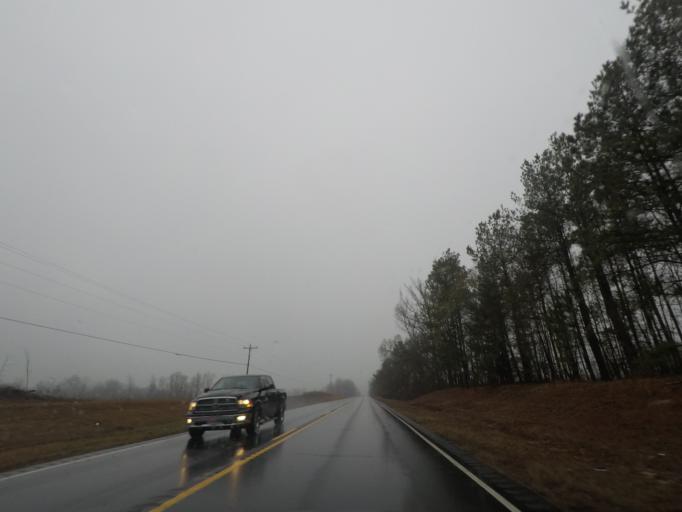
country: US
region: North Carolina
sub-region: Scotland County
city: Laurinburg
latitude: 34.8320
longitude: -79.4592
